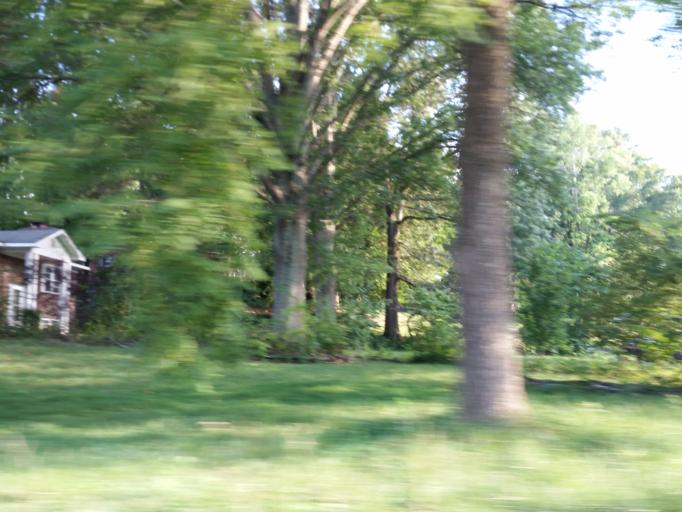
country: US
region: Tennessee
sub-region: Knox County
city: Knoxville
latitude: 35.8809
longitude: -83.9323
